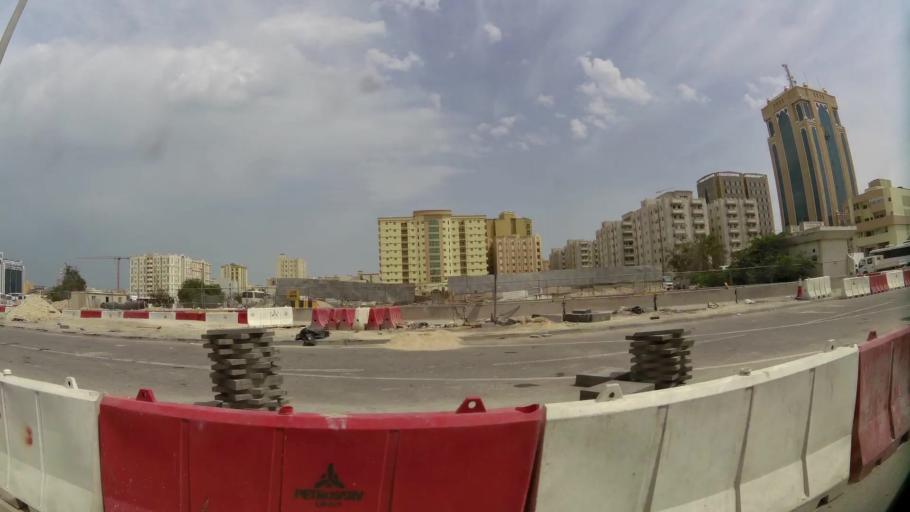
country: QA
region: Baladiyat ad Dawhah
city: Doha
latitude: 25.2765
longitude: 51.5284
